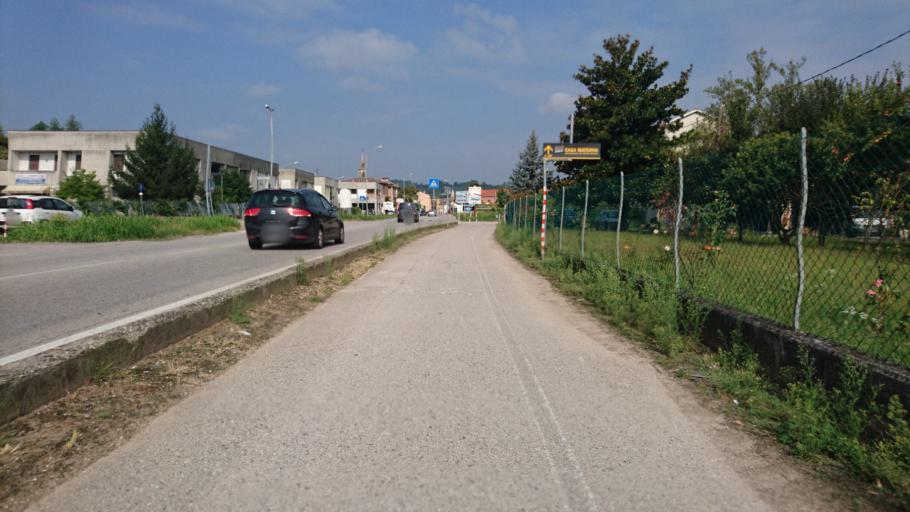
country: IT
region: Veneto
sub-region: Provincia di Vicenza
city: Arcugnano-Torri
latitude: 45.5023
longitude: 11.5745
